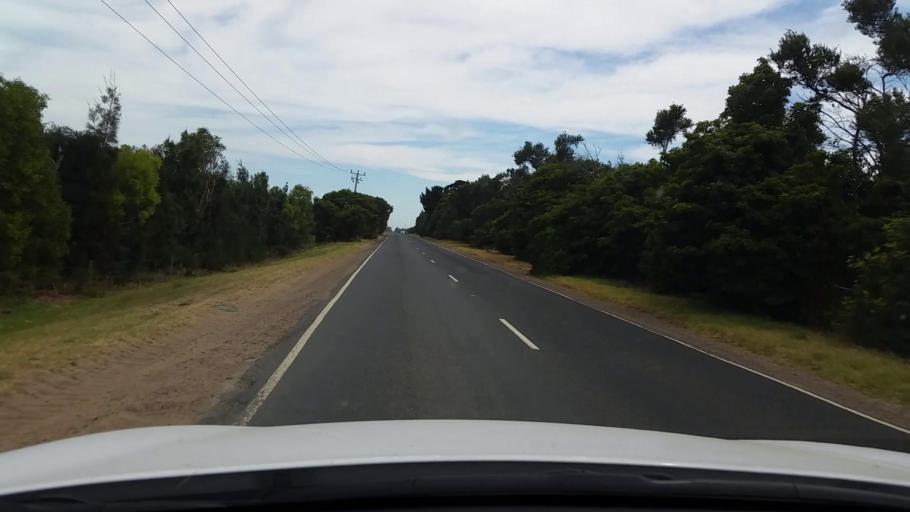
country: AU
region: Victoria
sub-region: Mornington Peninsula
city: Rosebud West
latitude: -38.4190
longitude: 144.8872
